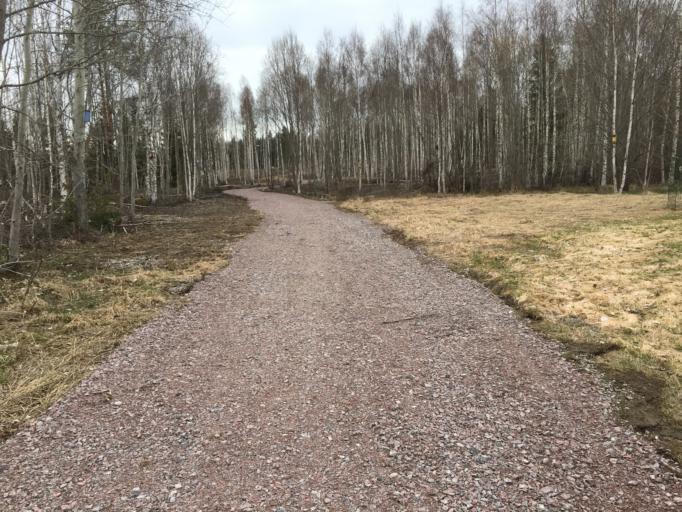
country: SE
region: Gaevleborg
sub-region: Hofors Kommun
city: Hofors
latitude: 60.5150
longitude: 16.4691
